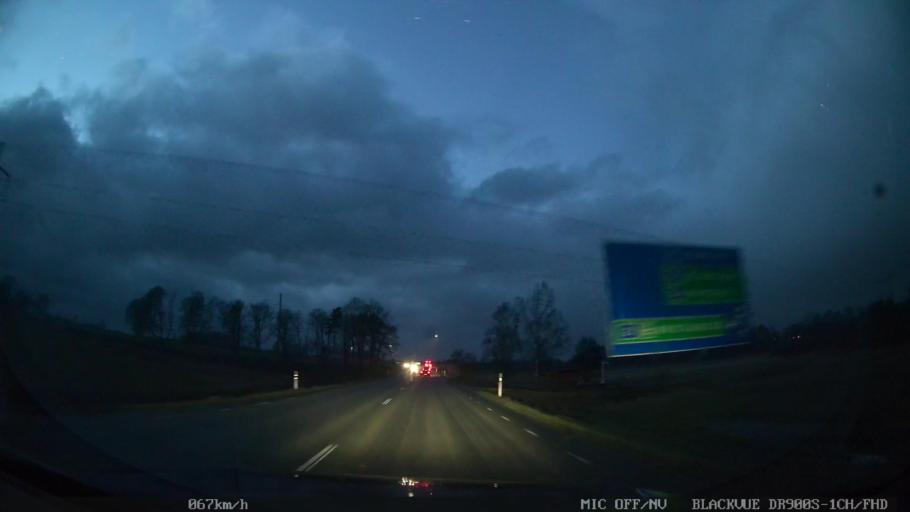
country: SE
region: Skane
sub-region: Hassleholms Kommun
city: Hassleholm
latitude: 56.1764
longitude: 13.7561
